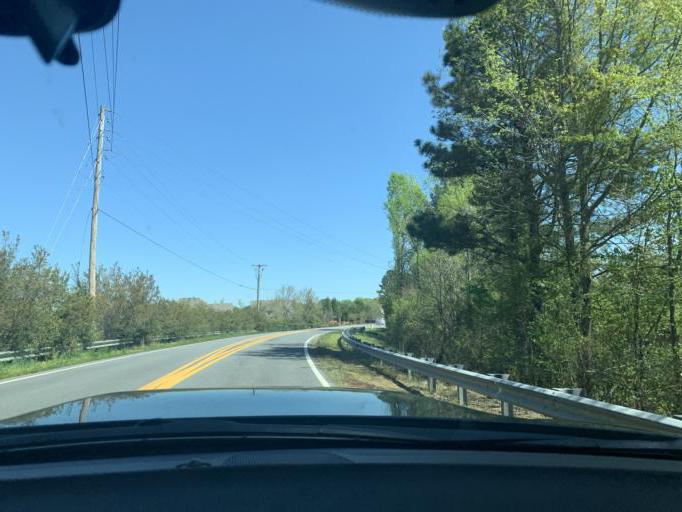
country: US
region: Georgia
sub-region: Fulton County
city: Milton
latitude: 34.1312
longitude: -84.2108
